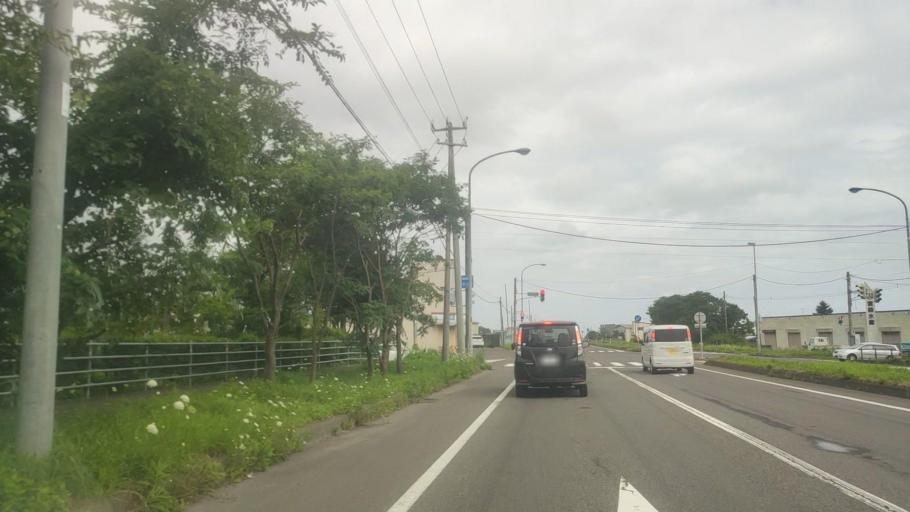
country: JP
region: Hokkaido
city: Shiraoi
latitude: 42.4631
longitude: 141.2160
